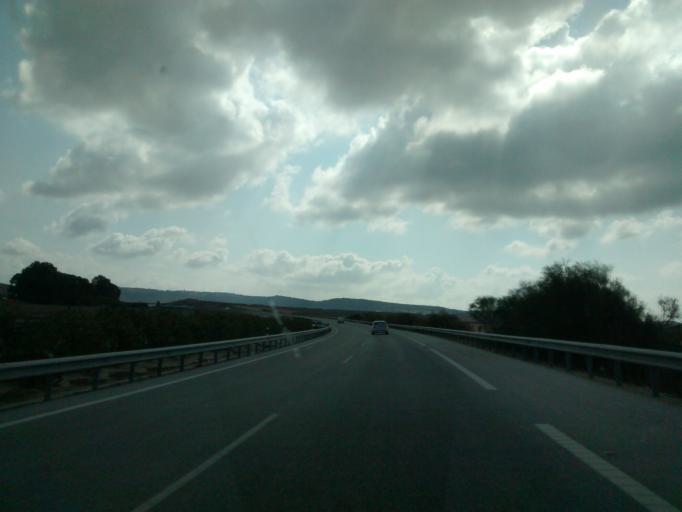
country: ES
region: Andalusia
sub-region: Provincia de Cadiz
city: Vejer de la Frontera
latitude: 36.2498
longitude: -6.0210
